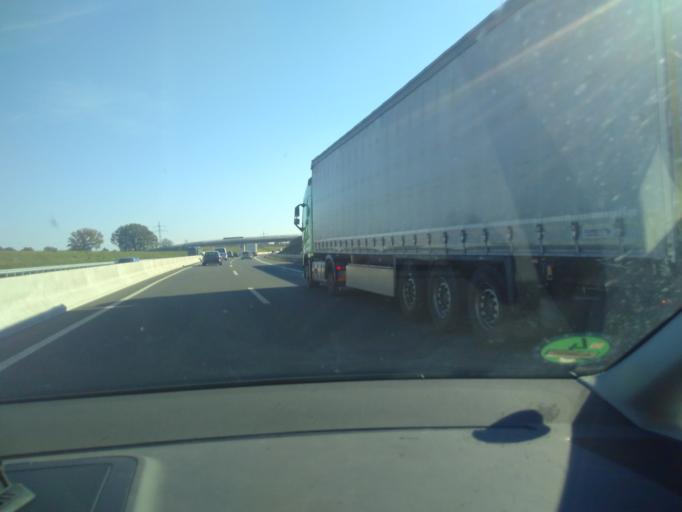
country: DE
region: North Rhine-Westphalia
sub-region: Regierungsbezirk Detmold
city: Steinhagen
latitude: 52.0047
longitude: 8.4378
